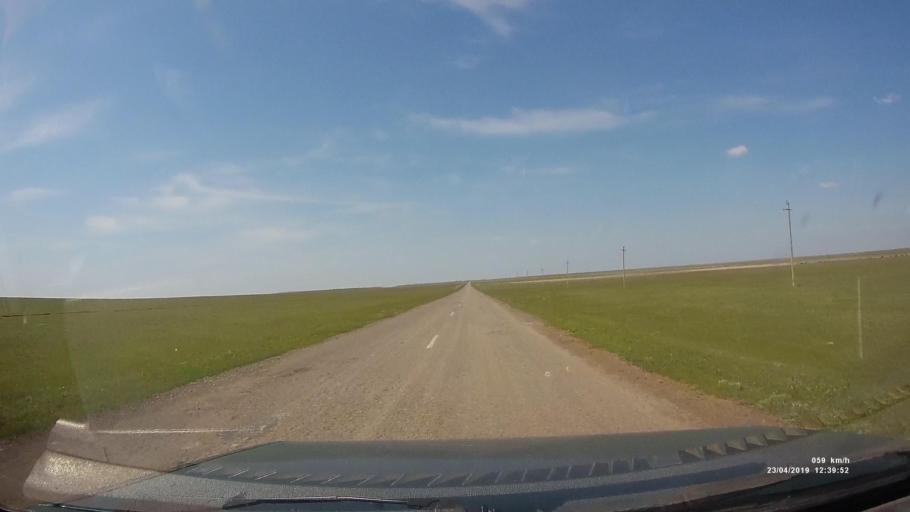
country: RU
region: Kalmykiya
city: Yashalta
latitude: 46.4366
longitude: 42.7039
